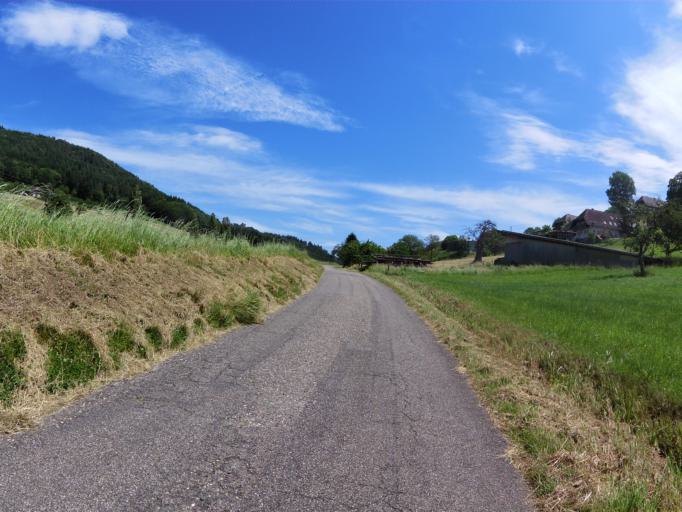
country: DE
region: Baden-Wuerttemberg
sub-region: Freiburg Region
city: Seelbach
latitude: 48.3215
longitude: 7.9457
